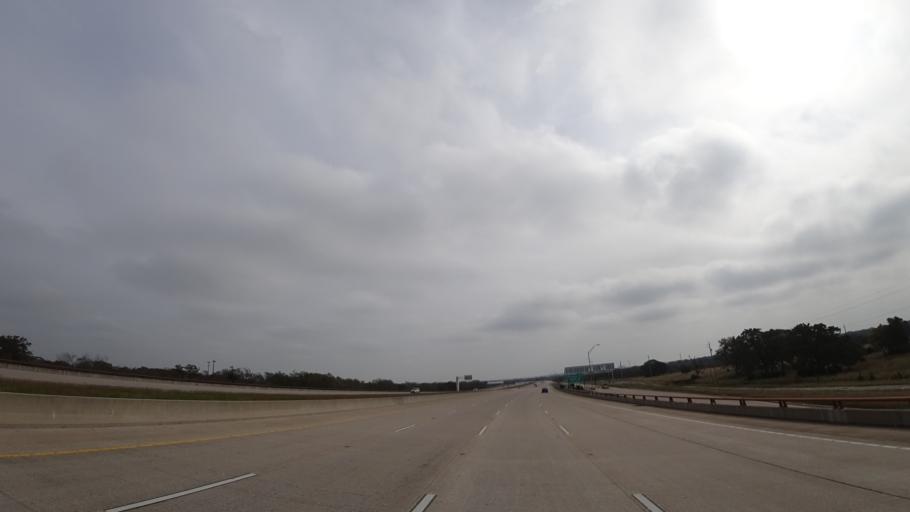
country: US
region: Texas
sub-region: Williamson County
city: Brushy Creek
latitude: 30.4809
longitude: -97.7401
